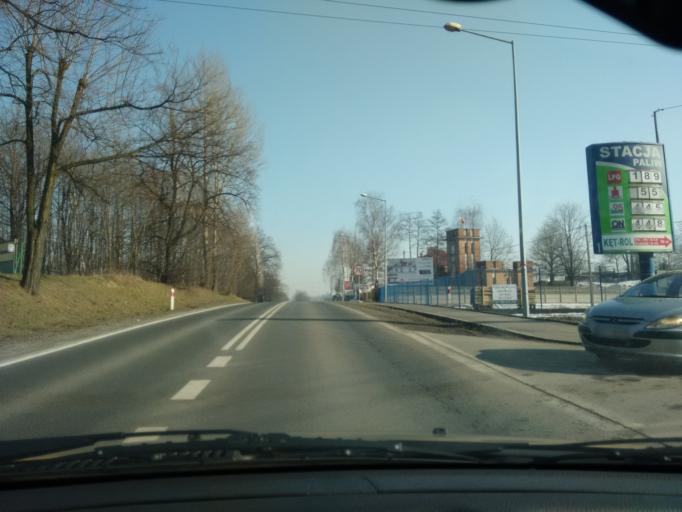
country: PL
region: Lesser Poland Voivodeship
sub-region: Powiat oswiecimski
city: Kety
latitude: 49.8822
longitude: 19.2414
